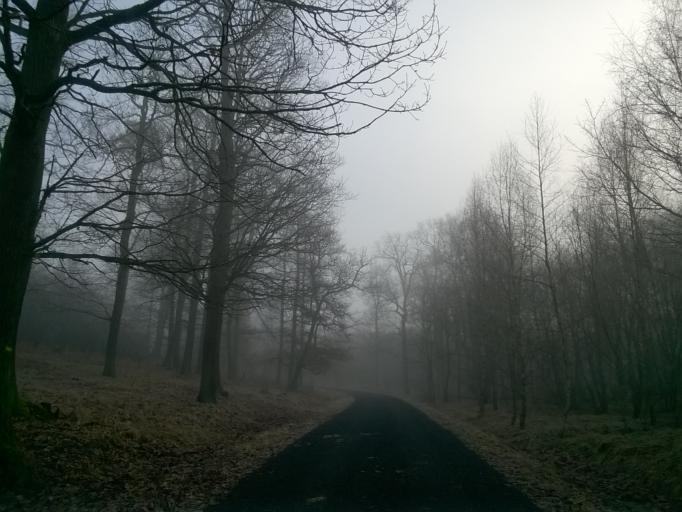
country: PL
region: Kujawsko-Pomorskie
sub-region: Powiat nakielski
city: Kcynia
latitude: 53.0486
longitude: 17.4804
